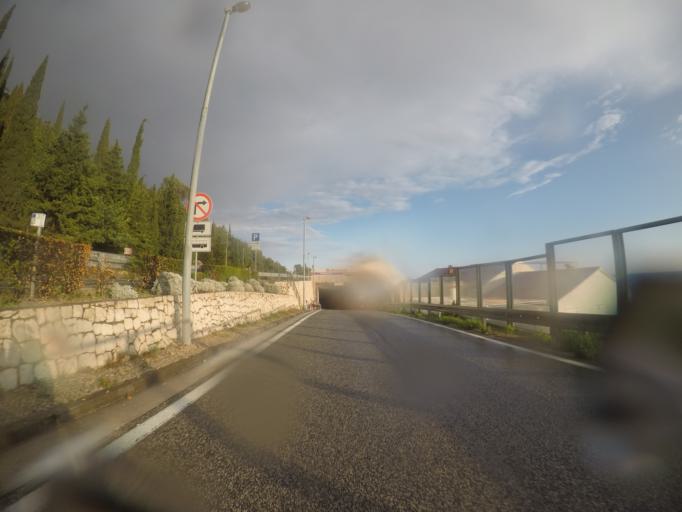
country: HR
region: Dubrovacko-Neretvanska
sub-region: Grad Dubrovnik
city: Dubrovnik
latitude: 42.6471
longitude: 18.1052
